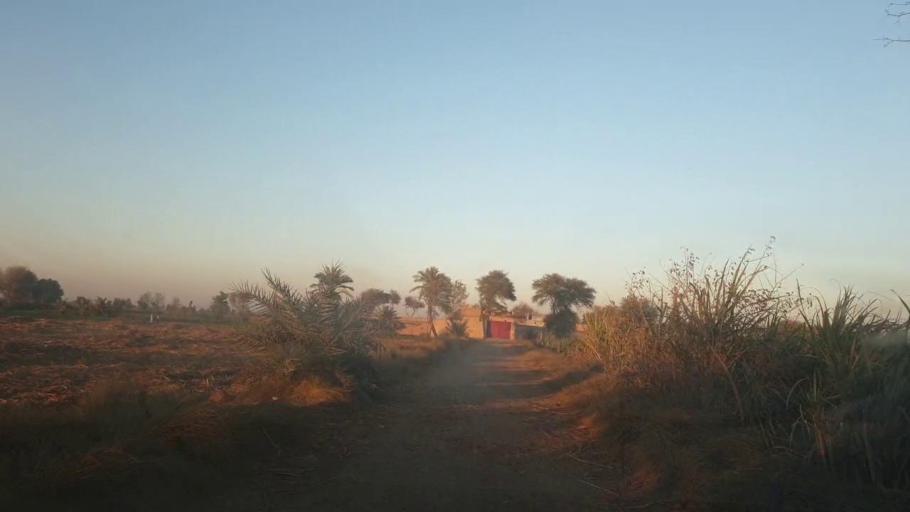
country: PK
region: Sindh
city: Ghotki
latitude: 28.0345
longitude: 69.2963
